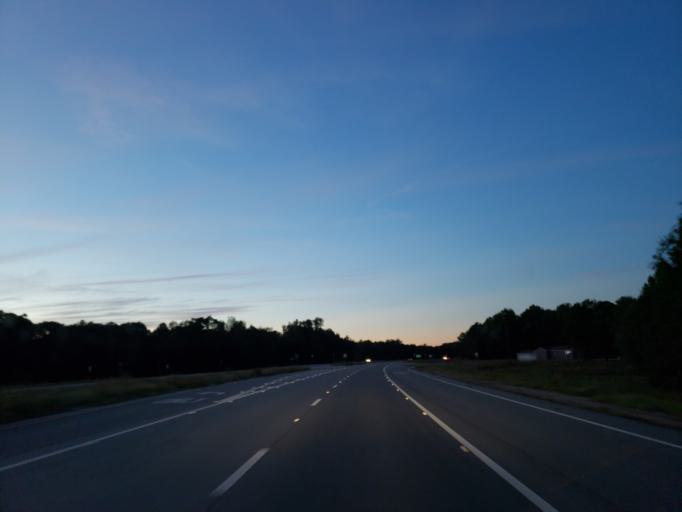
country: US
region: Mississippi
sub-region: Wayne County
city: Waynesboro
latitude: 31.8493
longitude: -88.7166
